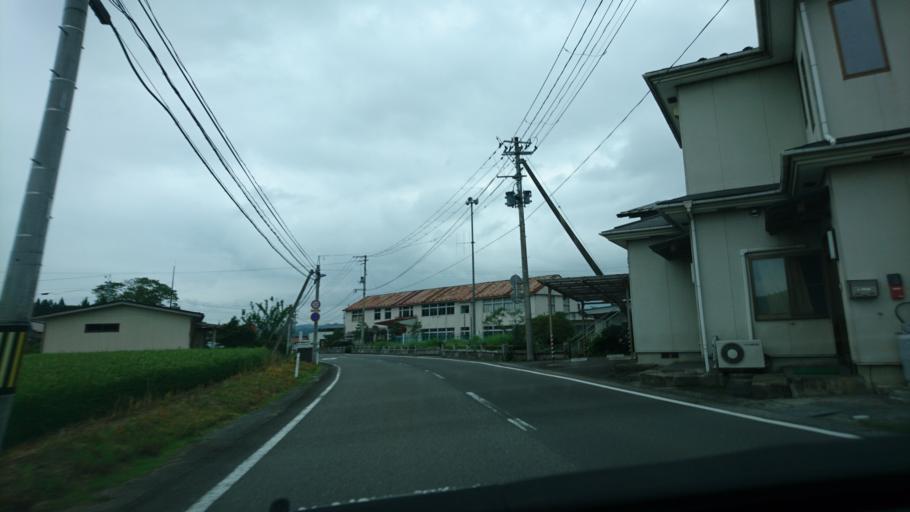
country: JP
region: Iwate
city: Ichinoseki
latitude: 38.8058
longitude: 140.9432
